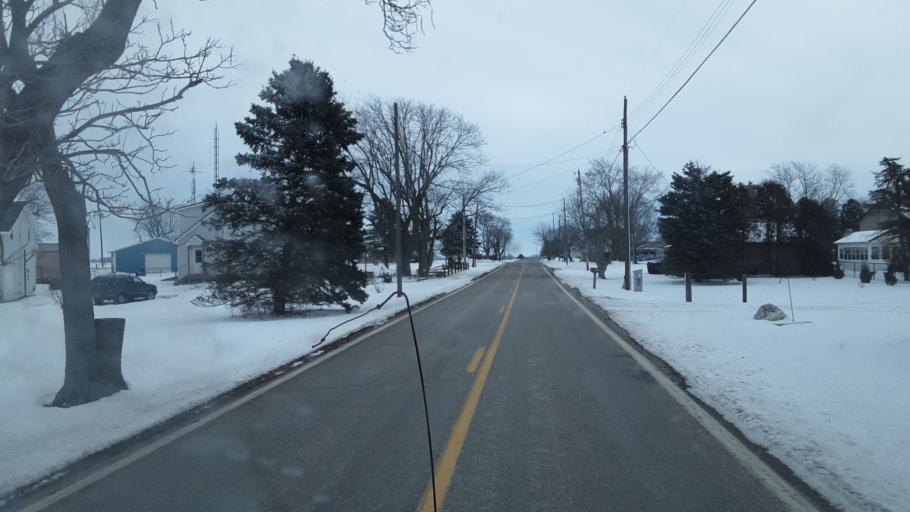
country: US
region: Ohio
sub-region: Madison County
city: Bethel
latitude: 39.7321
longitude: -83.4275
